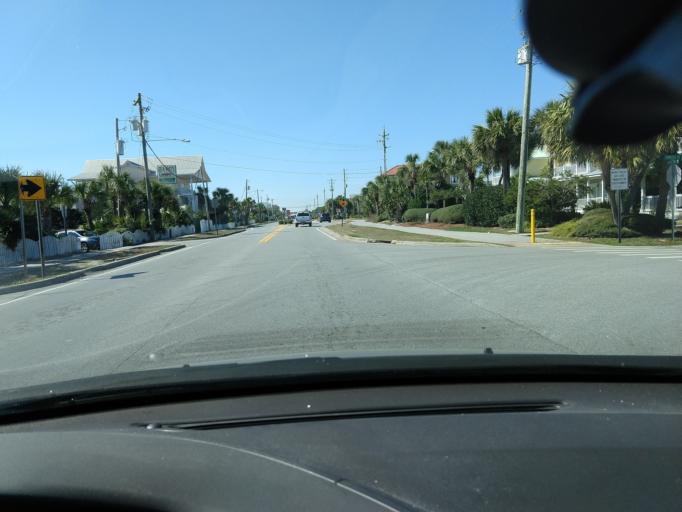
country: US
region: Florida
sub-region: Walton County
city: Miramar Beach
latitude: 30.3815
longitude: -86.4148
